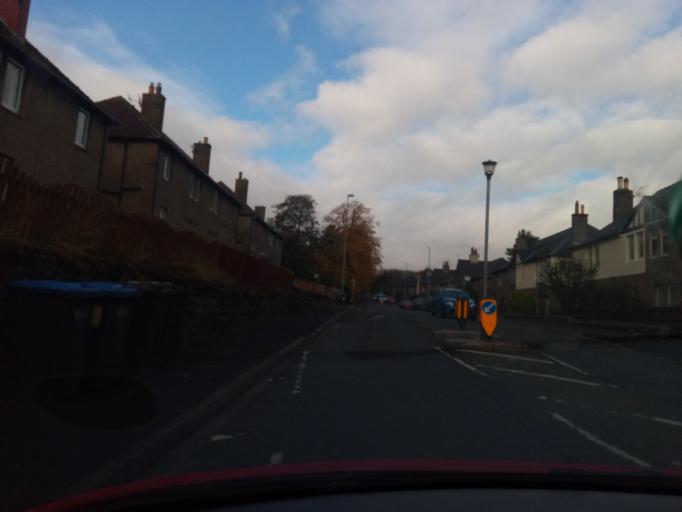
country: GB
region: Scotland
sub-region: The Scottish Borders
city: Galashiels
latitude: 55.6255
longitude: -2.8310
